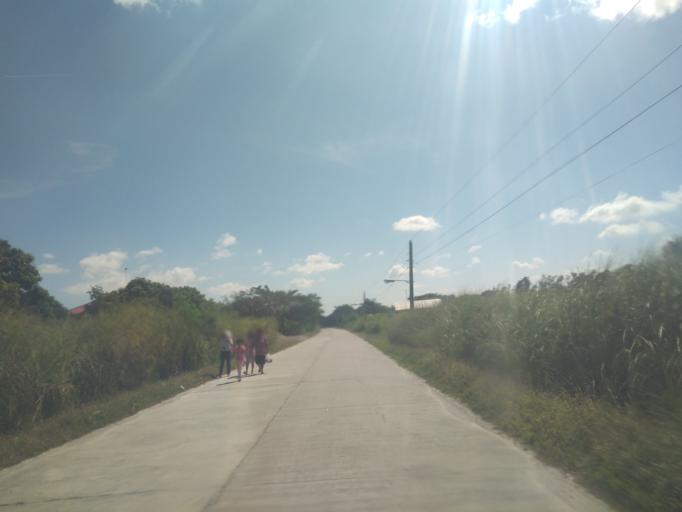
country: PH
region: Central Luzon
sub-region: Province of Pampanga
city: Balas
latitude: 15.0531
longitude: 120.6068
